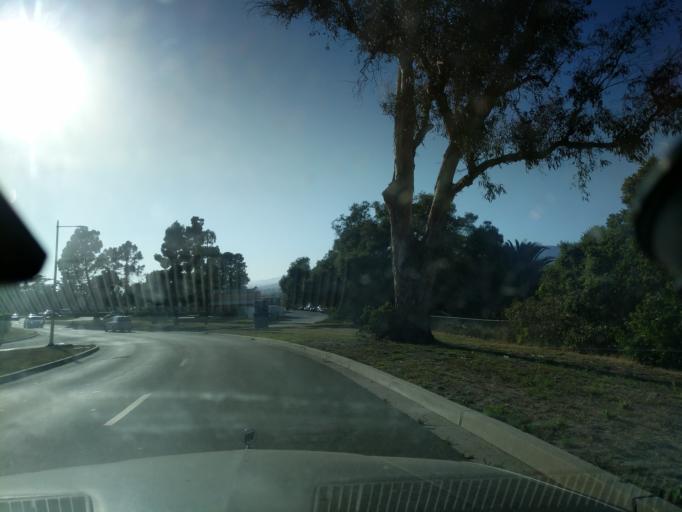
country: US
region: California
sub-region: Santa Barbara County
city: Isla Vista
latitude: 34.4213
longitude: -119.8514
